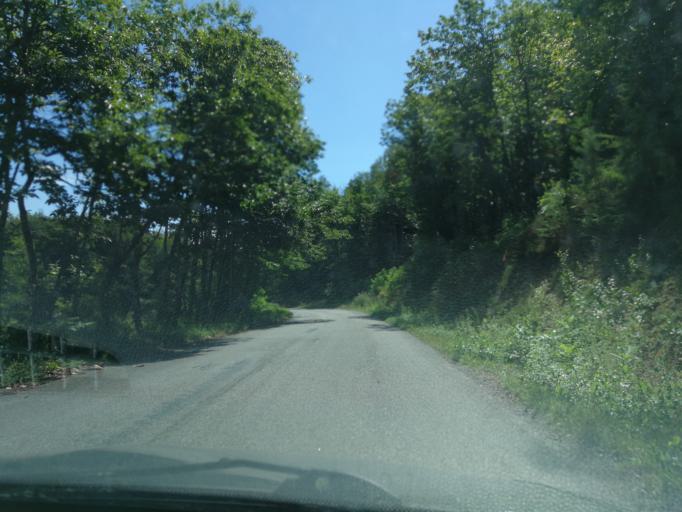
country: FR
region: Limousin
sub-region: Departement de la Correze
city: Argentat
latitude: 45.1067
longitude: 1.8708
